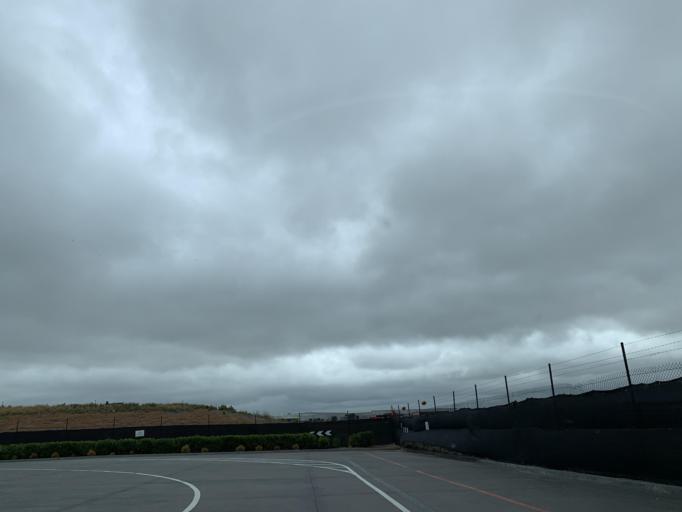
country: AU
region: Victoria
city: Heatherton
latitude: -37.9717
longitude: 145.0936
